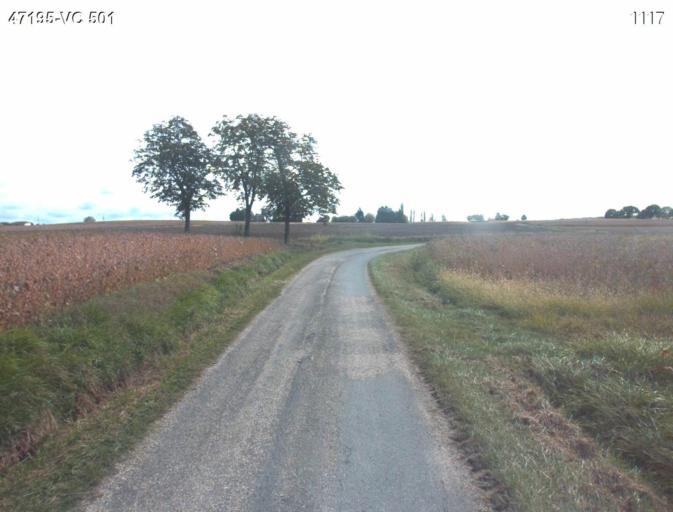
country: FR
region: Aquitaine
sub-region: Departement du Lot-et-Garonne
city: Nerac
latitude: 44.1004
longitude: 0.3212
